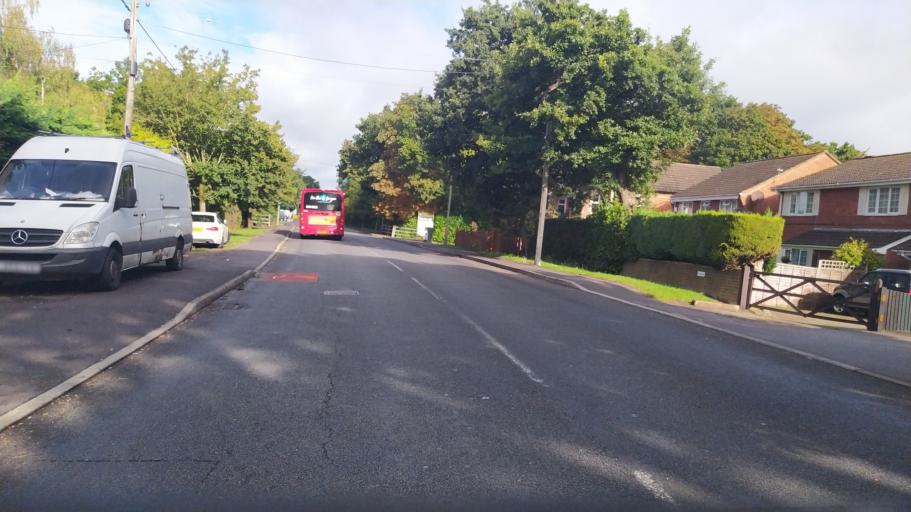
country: GB
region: England
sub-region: Hampshire
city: Totton
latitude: 50.9310
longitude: -1.5046
